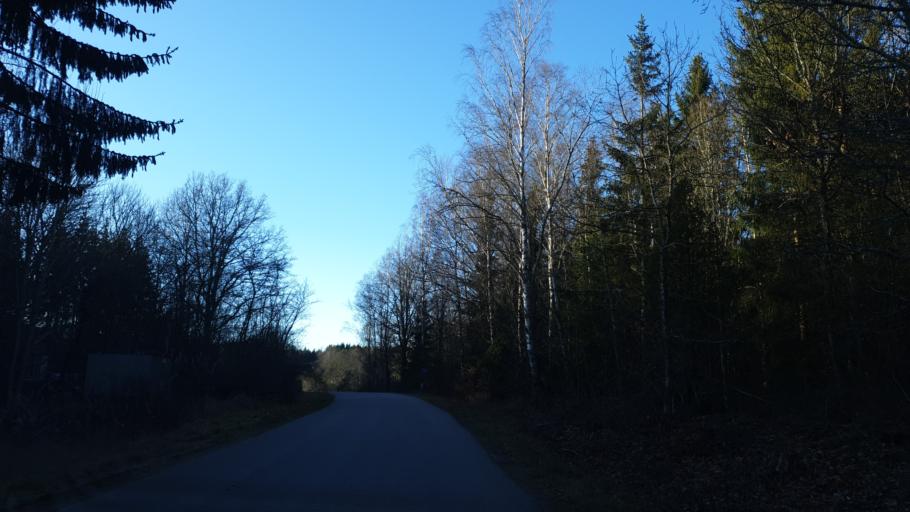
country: SE
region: Blekinge
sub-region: Karlskrona Kommun
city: Nattraby
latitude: 56.2619
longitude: 15.4931
